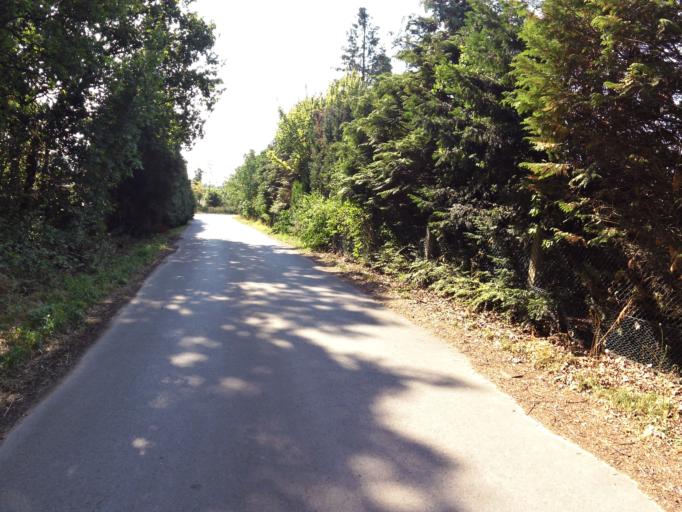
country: DE
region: North Rhine-Westphalia
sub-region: Regierungsbezirk Detmold
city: Harsewinkel
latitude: 51.9385
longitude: 8.2553
